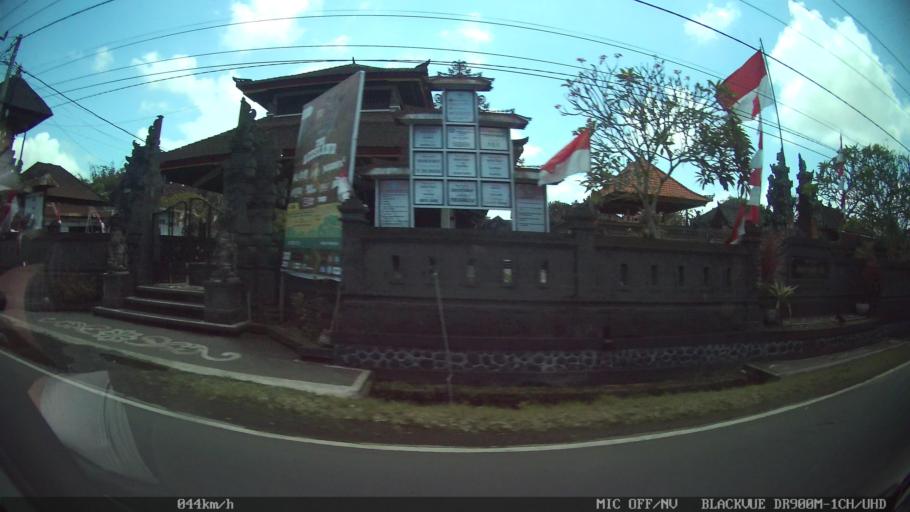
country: ID
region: Bali
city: Banjar Jabejero
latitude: -8.5923
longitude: 115.2615
